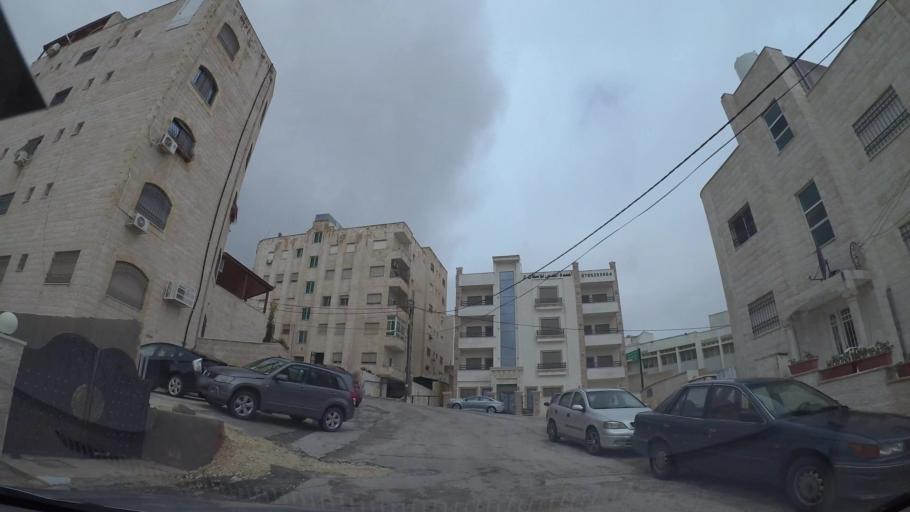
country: JO
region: Amman
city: Al Jubayhah
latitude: 32.0584
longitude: 35.8907
